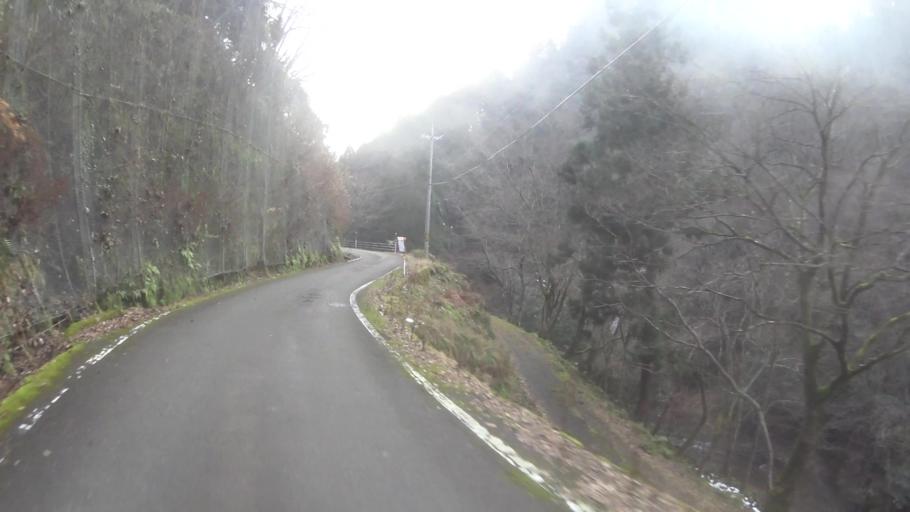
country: JP
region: Kyoto
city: Maizuru
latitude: 35.3642
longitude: 135.4653
